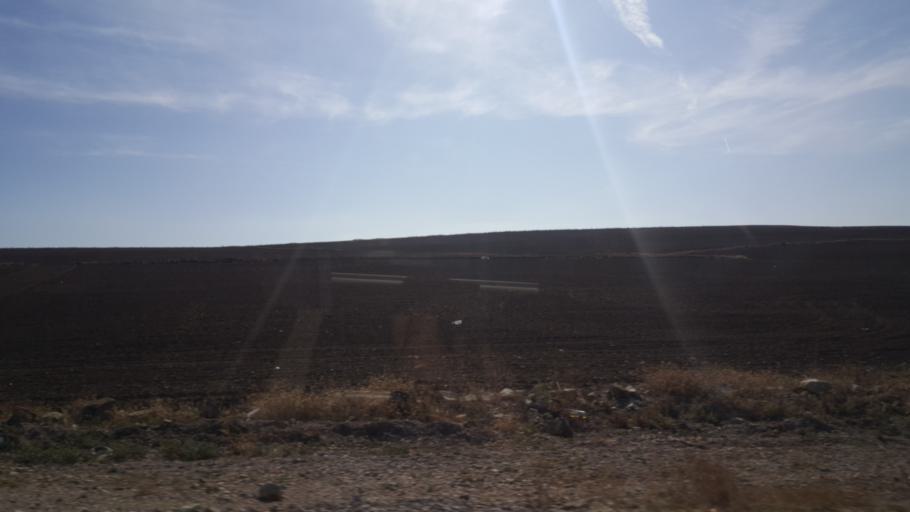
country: TR
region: Ankara
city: Haymana
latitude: 39.4013
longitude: 32.6239
